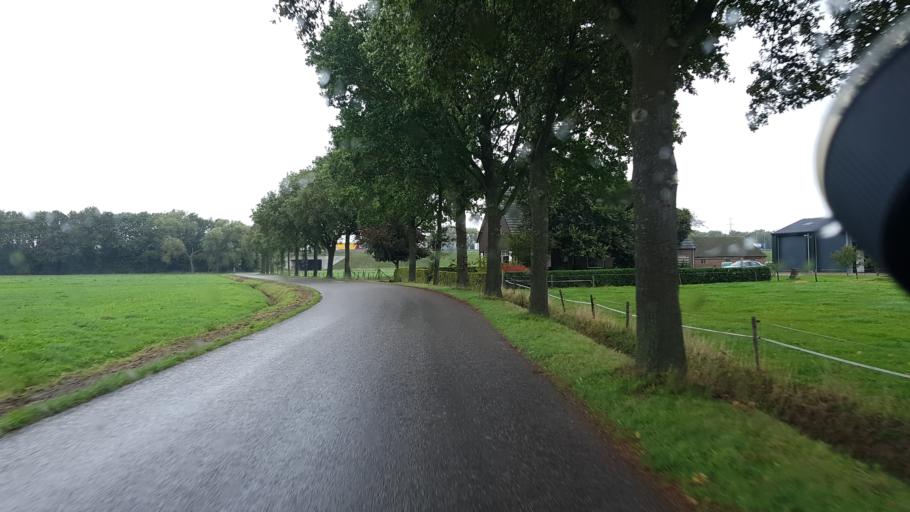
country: NL
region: Gelderland
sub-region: Gemeente Apeldoorn
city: Apeldoorn
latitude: 52.1884
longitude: 6.0320
